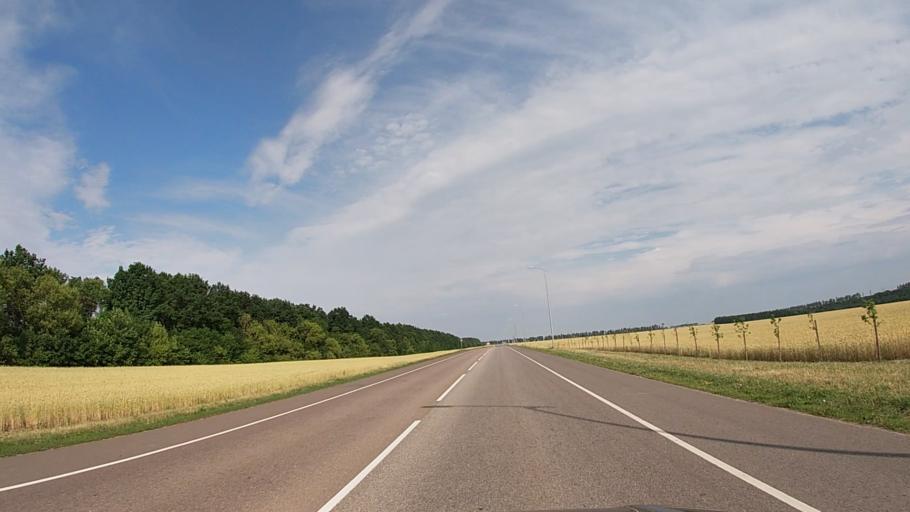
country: RU
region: Belgorod
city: Proletarskiy
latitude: 50.8255
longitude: 35.7806
